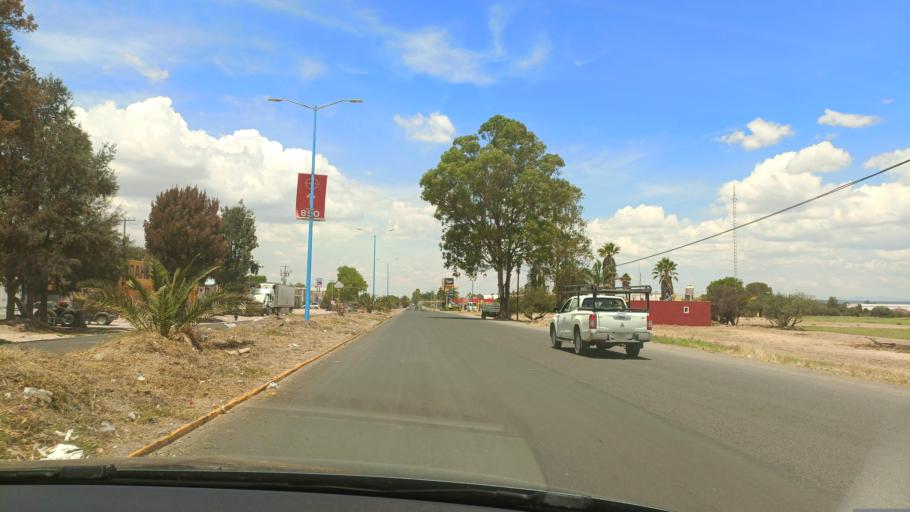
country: MX
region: Guanajuato
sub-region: San Luis de la Paz
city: San Ignacio
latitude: 21.2930
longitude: -100.5387
